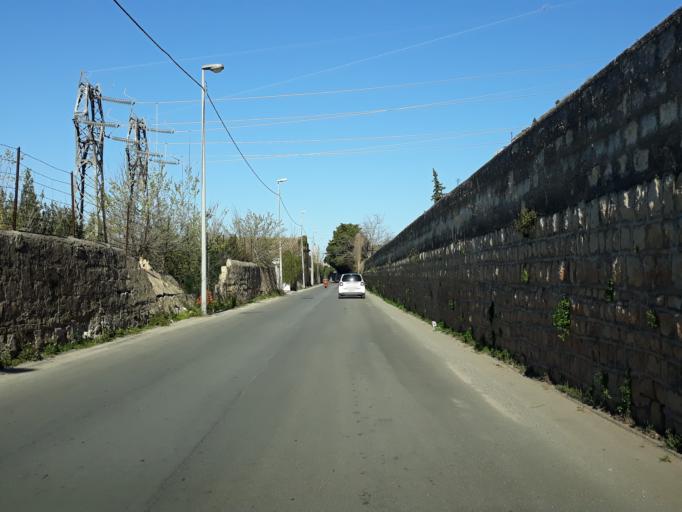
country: IT
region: Sicily
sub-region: Palermo
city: Ciaculli
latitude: 38.0851
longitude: 13.3787
